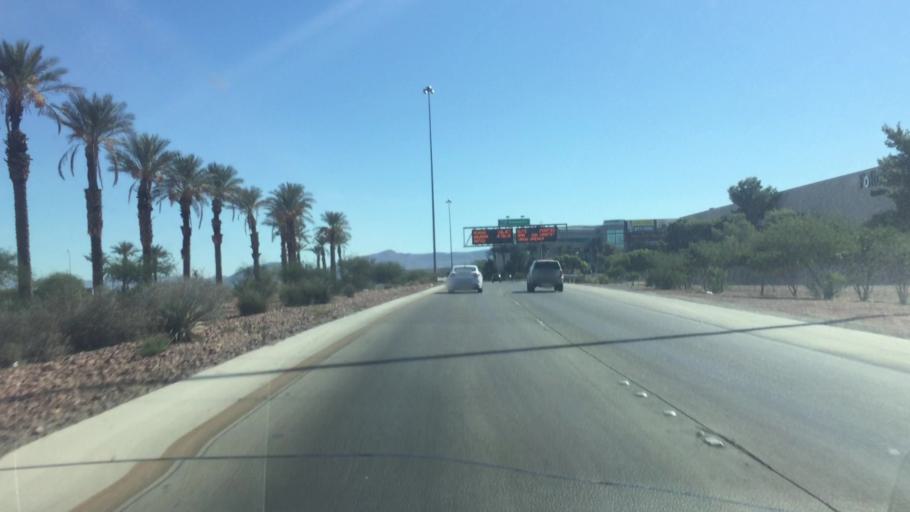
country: US
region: Nevada
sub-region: Clark County
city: Paradise
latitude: 36.0628
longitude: -115.1566
